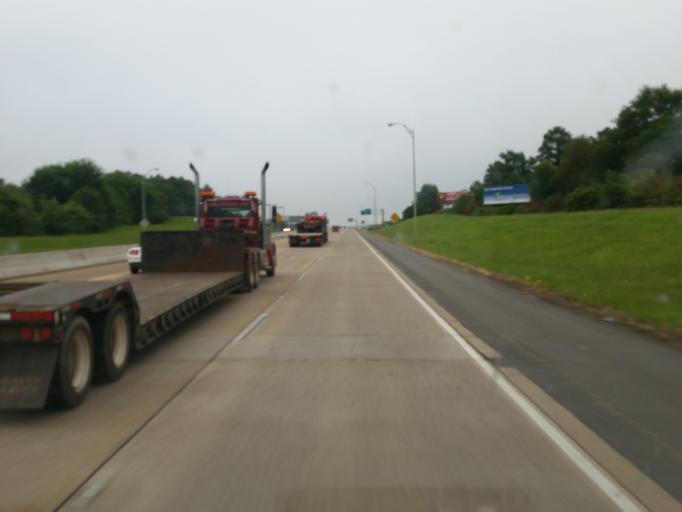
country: US
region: Louisiana
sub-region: Caddo Parish
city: Shreveport
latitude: 32.4703
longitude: -93.8031
